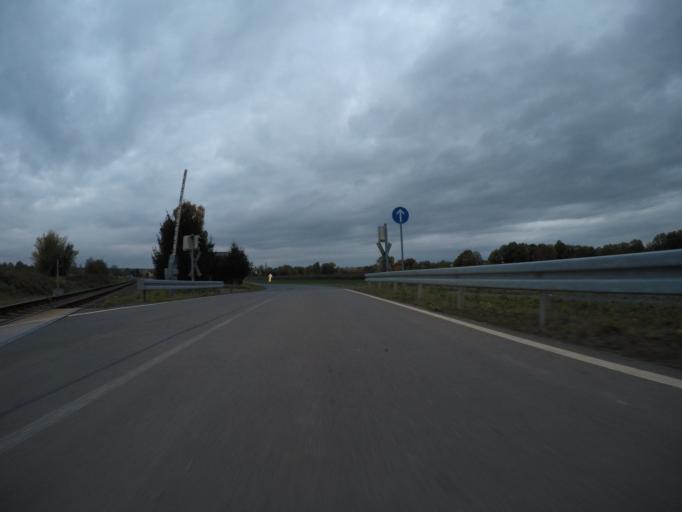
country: DE
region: Thuringia
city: Saara
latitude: 50.9270
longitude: 12.4268
